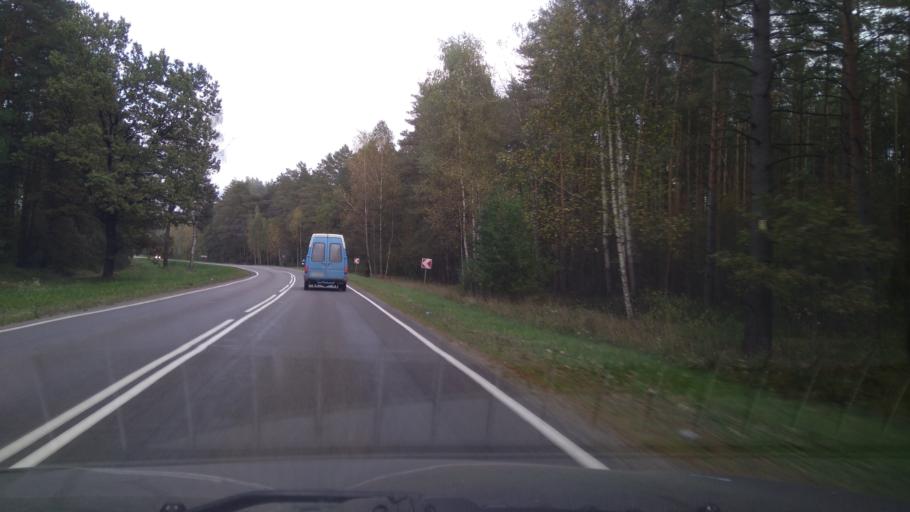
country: BY
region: Minsk
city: Svislach
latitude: 53.6403
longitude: 27.9064
